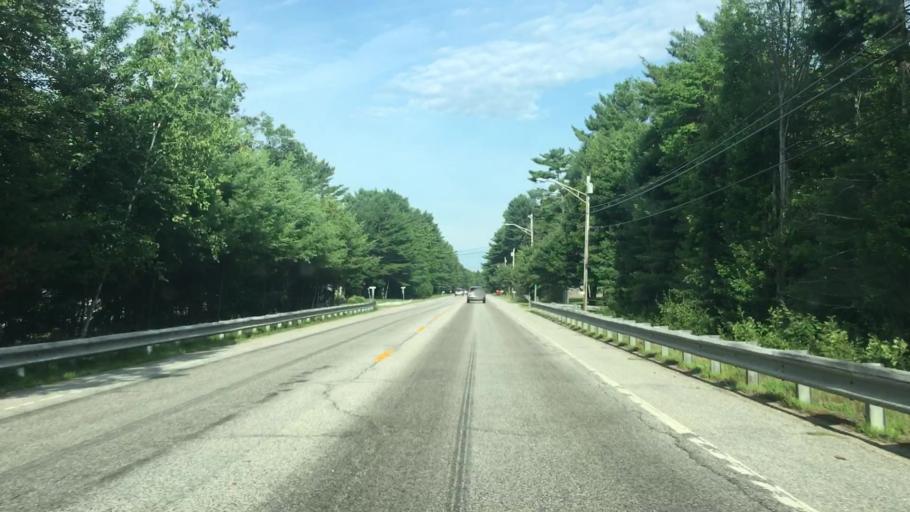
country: US
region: Maine
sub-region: Cumberland County
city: Steep Falls
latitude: 43.7323
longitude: -70.6053
